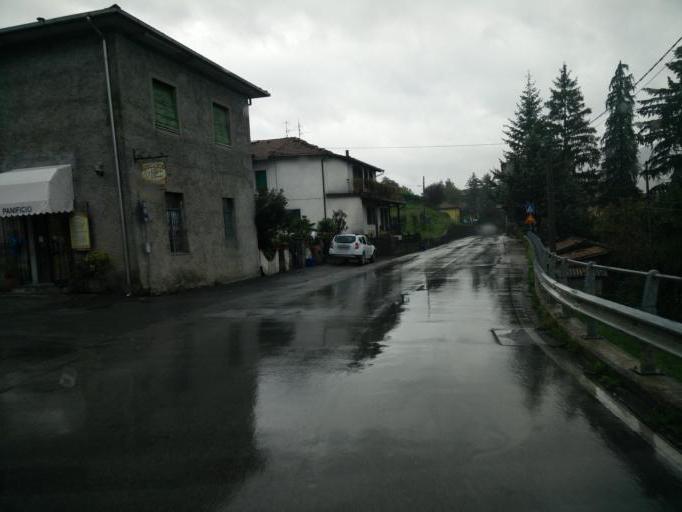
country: IT
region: Tuscany
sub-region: Provincia di Lucca
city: San Romano in Garfagnana
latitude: 44.1642
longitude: 10.3542
